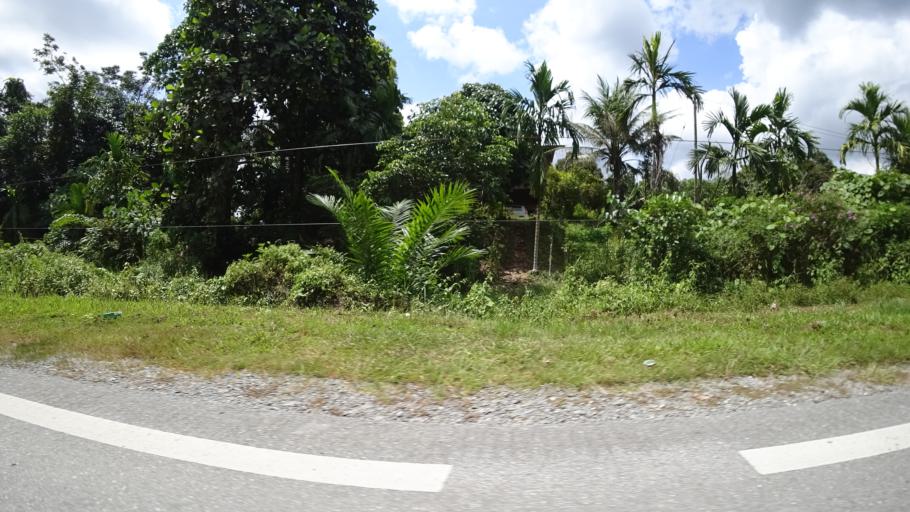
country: BN
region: Tutong
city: Tutong
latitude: 4.7034
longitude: 114.7989
